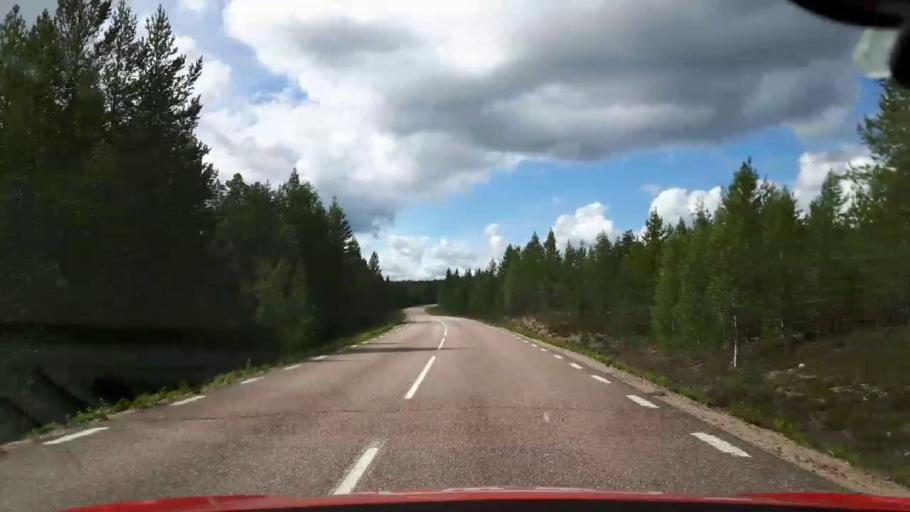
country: SE
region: Jaemtland
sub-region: Harjedalens Kommun
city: Sveg
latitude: 61.8322
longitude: 13.8929
